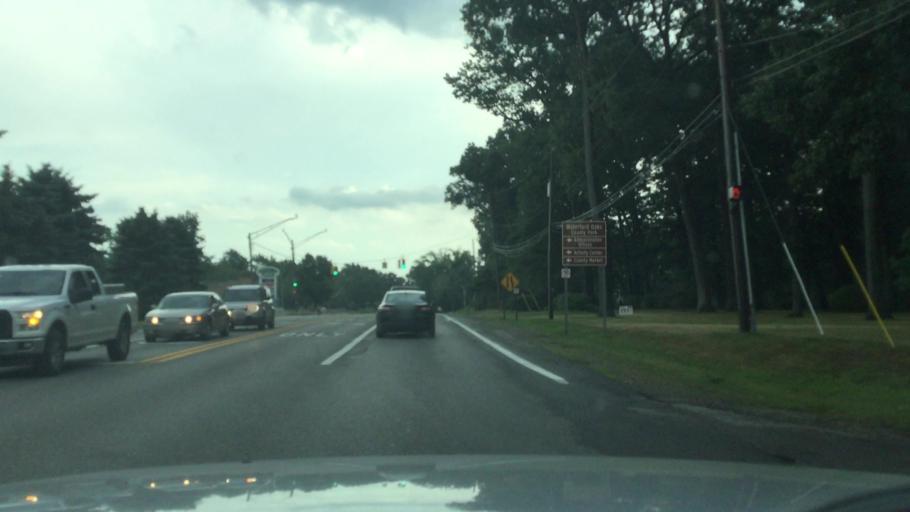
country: US
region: Michigan
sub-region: Oakland County
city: Sylvan Lake
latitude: 42.6621
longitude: -83.3469
